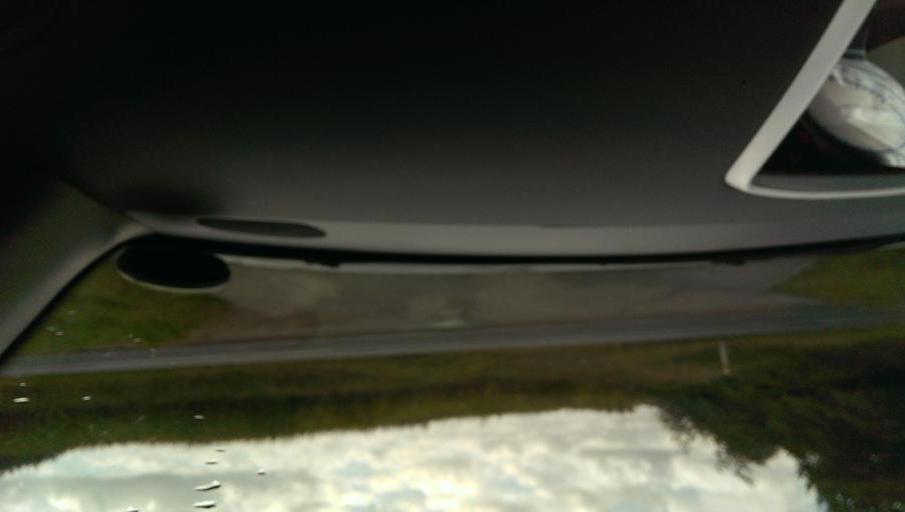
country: DK
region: South Denmark
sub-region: Varde Kommune
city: Varde
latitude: 55.6038
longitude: 8.4520
